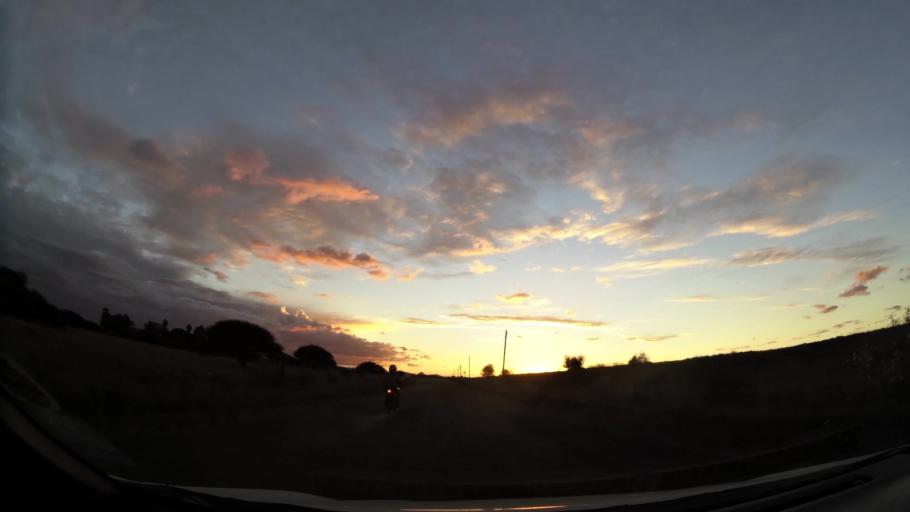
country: ZA
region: Limpopo
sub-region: Capricorn District Municipality
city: Polokwane
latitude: -23.7392
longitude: 29.4488
